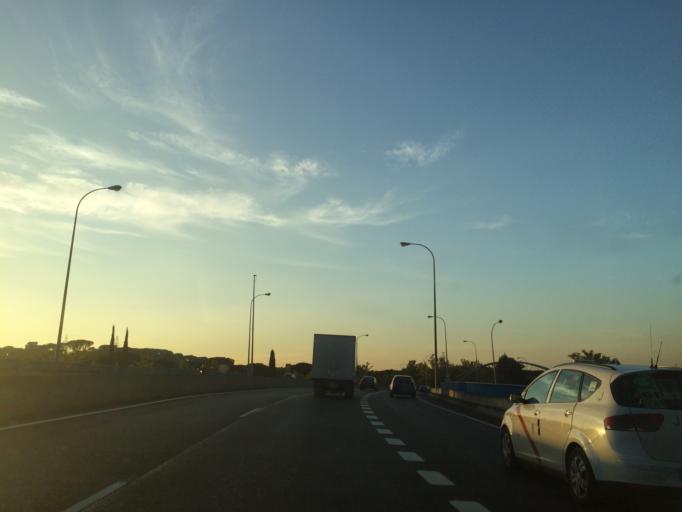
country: ES
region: Madrid
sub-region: Provincia de Madrid
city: Moncloa-Aravaca
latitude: 40.4345
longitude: -3.7376
